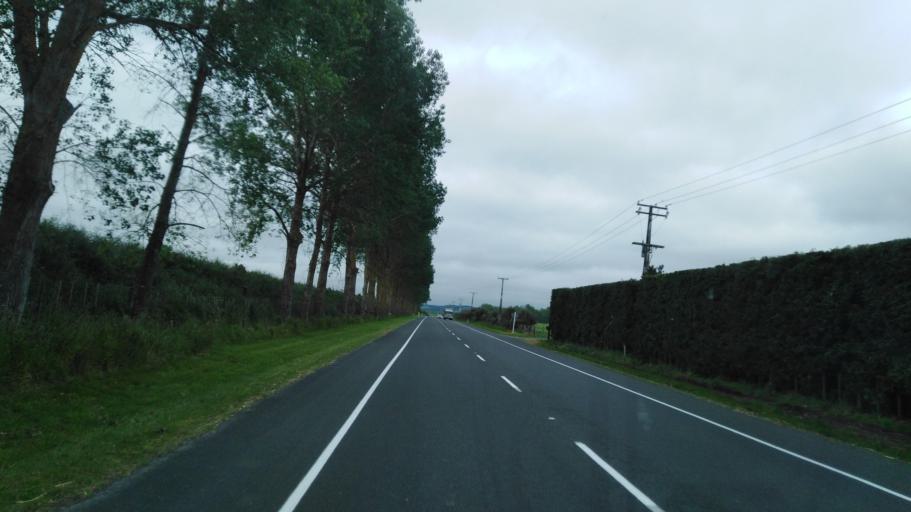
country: NZ
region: Waikato
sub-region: Taupo District
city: Taupo
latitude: -38.6122
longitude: 176.2697
